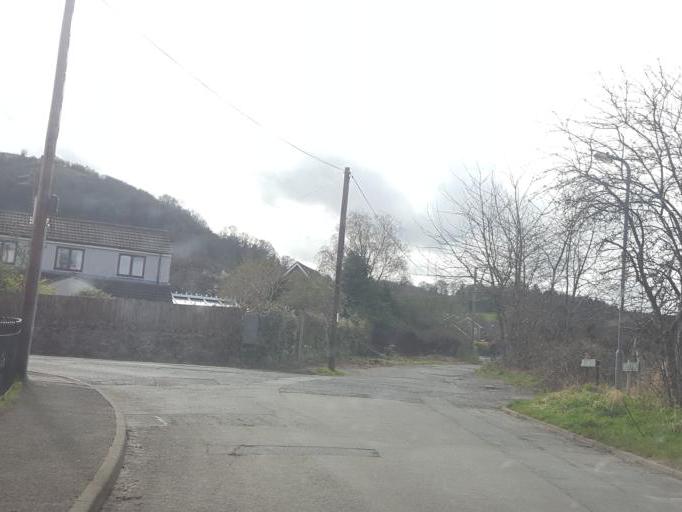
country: GB
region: England
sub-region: Worcestershire
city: Great Malvern
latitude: 52.1289
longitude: -2.3357
